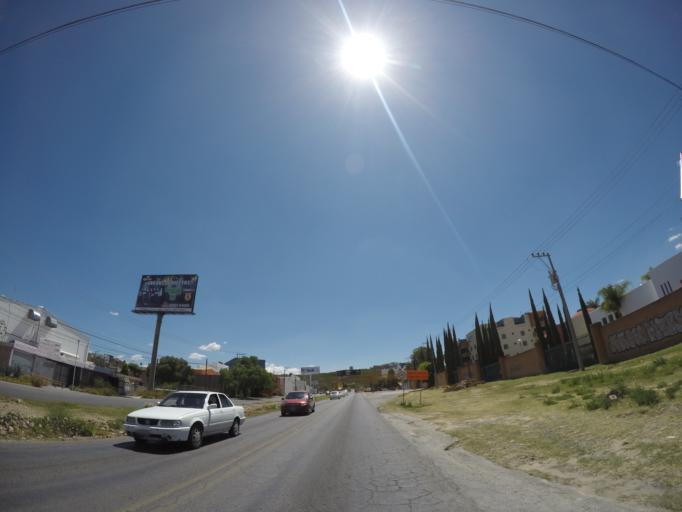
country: MX
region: San Luis Potosi
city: Escalerillas
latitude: 22.1306
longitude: -101.0362
